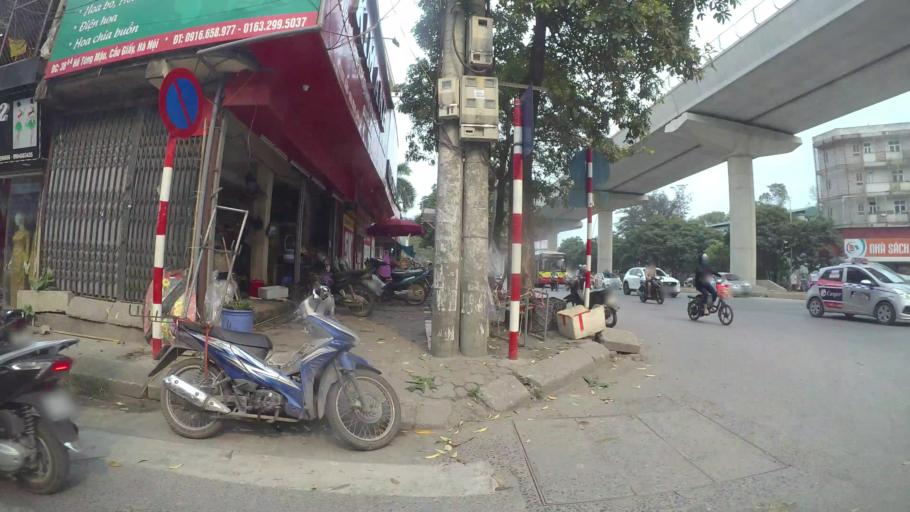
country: VN
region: Ha Noi
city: Cau Dien
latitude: 21.0380
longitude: 105.7739
